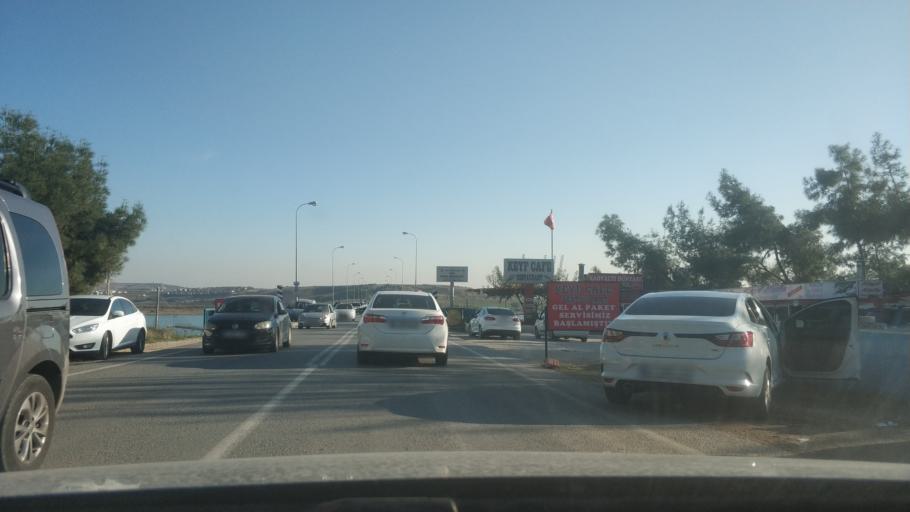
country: TR
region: Adana
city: Adana
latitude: 37.1044
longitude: 35.2990
